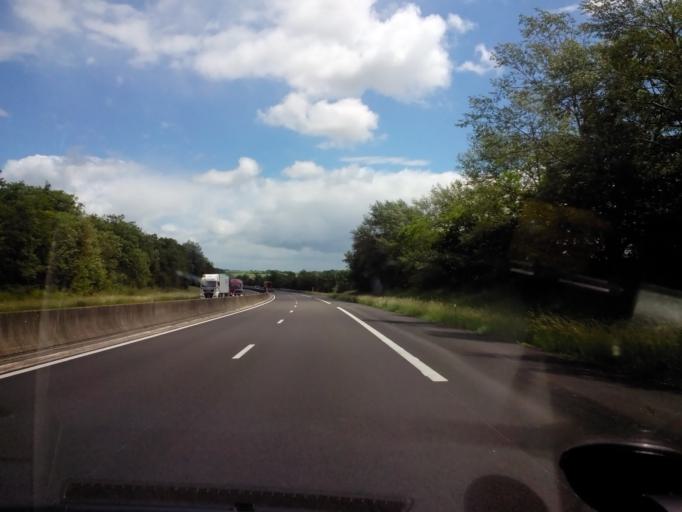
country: FR
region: Champagne-Ardenne
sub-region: Departement de la Haute-Marne
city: Avrecourt
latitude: 47.9524
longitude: 5.4316
